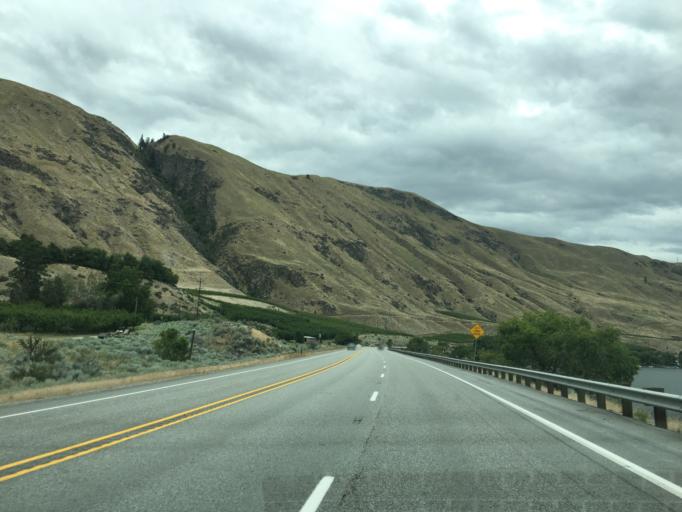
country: US
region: Washington
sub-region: Chelan County
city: Sunnyslope
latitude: 47.5552
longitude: -120.2547
